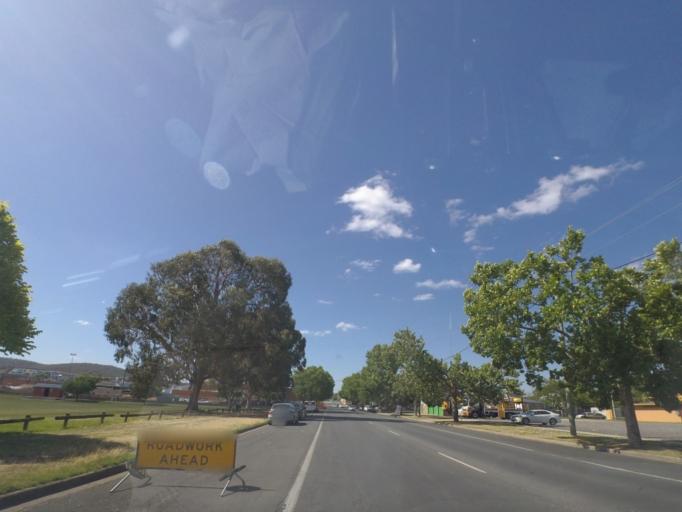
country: AU
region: New South Wales
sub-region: Albury Municipality
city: South Albury
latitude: -36.0867
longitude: 146.9145
